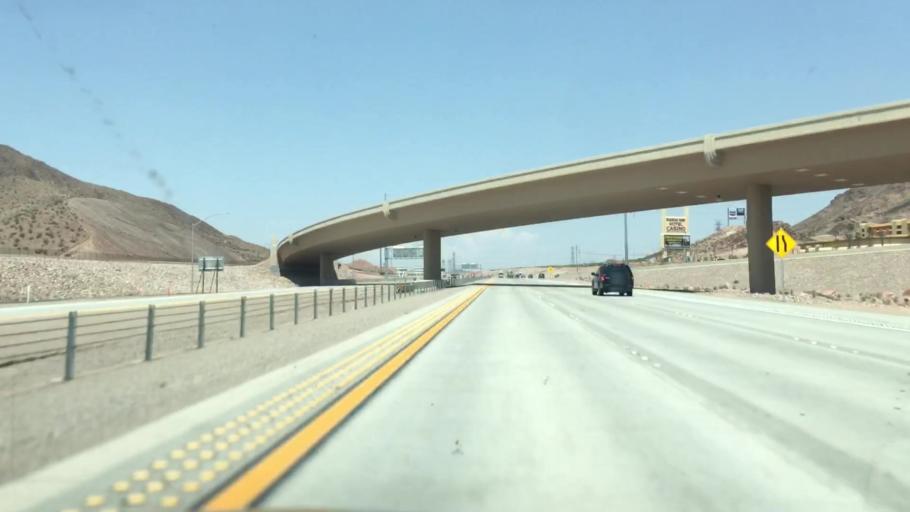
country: US
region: Nevada
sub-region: Clark County
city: Boulder City
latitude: 35.9682
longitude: -114.9129
